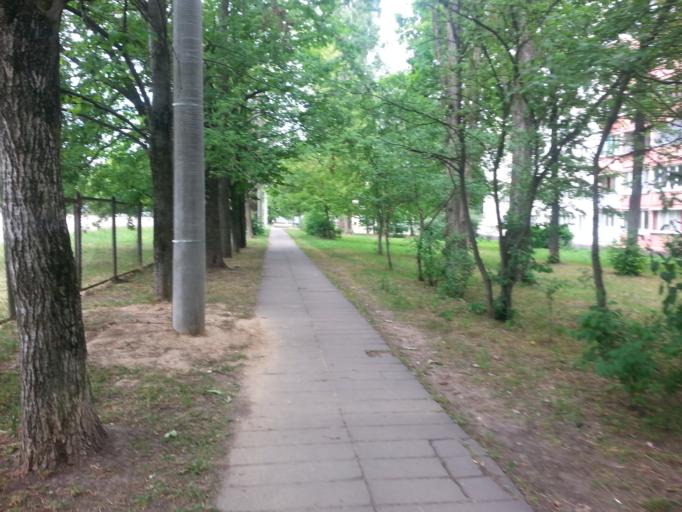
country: BY
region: Minsk
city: Novoye Medvezhino
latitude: 53.9141
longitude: 27.4914
